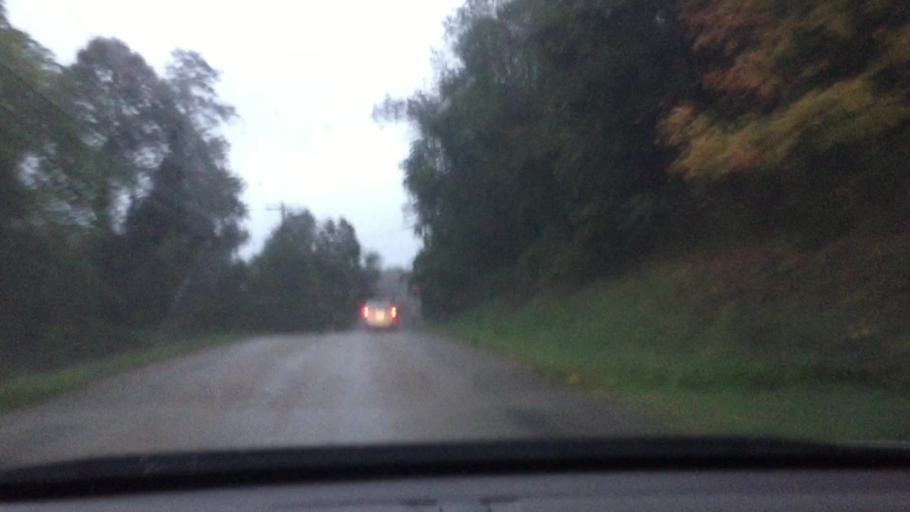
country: US
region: Pennsylvania
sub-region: Washington County
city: Bentleyville
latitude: 40.1298
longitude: -79.9683
